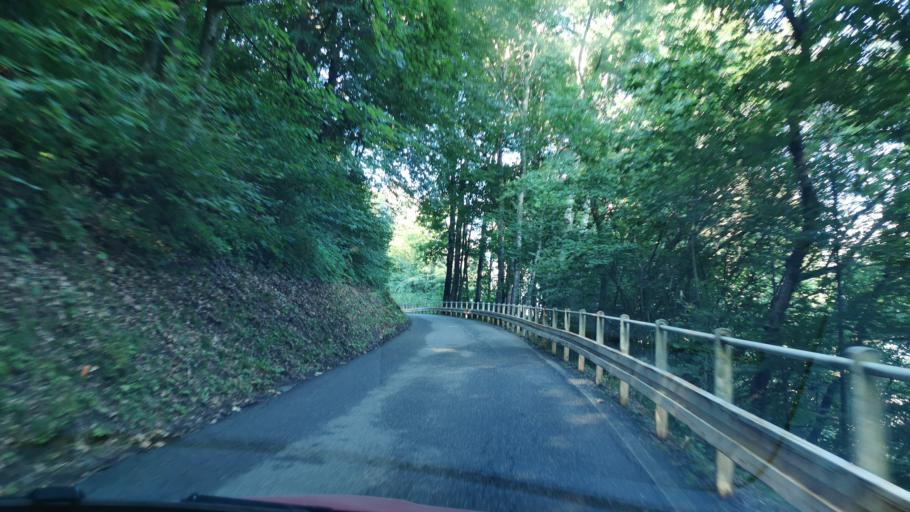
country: IT
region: Lombardy
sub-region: Provincia di Lecco
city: Moggio
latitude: 45.9241
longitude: 9.4924
